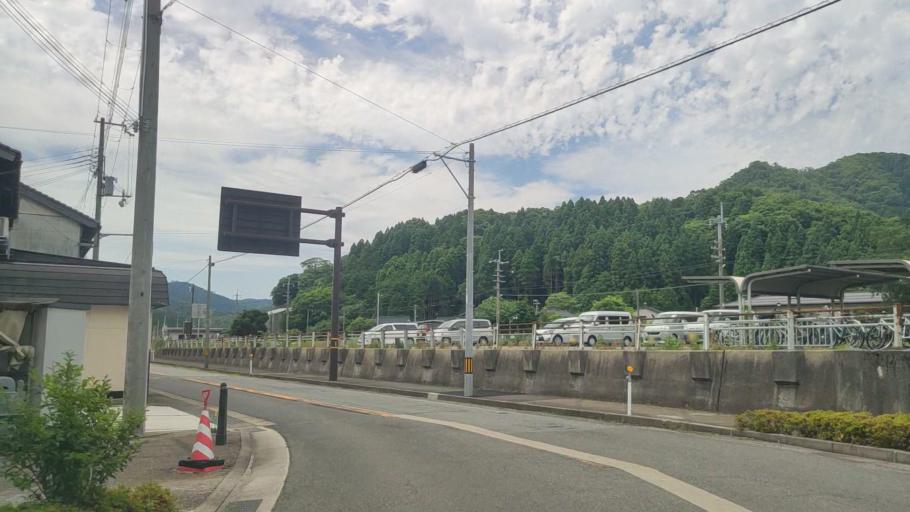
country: JP
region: Hyogo
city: Toyooka
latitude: 35.6500
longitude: 134.7569
